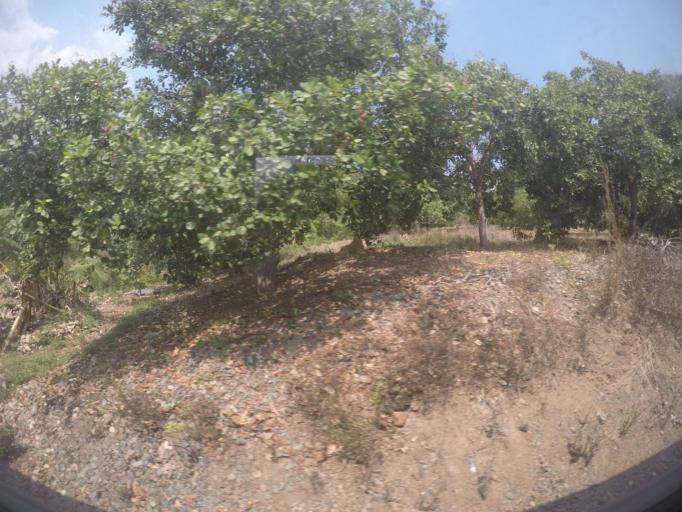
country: VN
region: Binh Thuan
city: Thuan Nam
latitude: 10.8827
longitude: 107.7060
